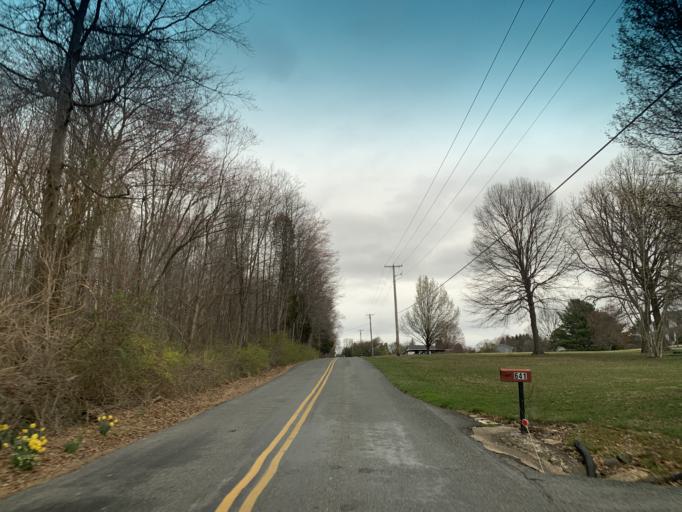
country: US
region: Maryland
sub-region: Harford County
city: Aberdeen
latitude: 39.5480
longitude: -76.1944
